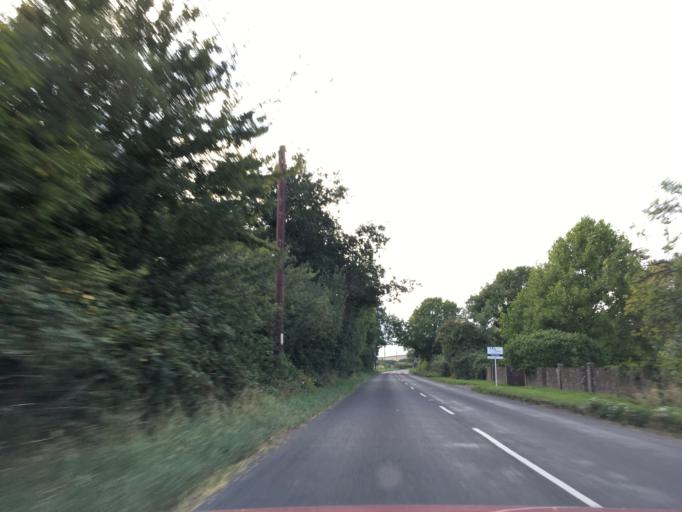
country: GB
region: England
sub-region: Wiltshire
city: Market Lavington
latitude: 51.3226
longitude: -1.9286
